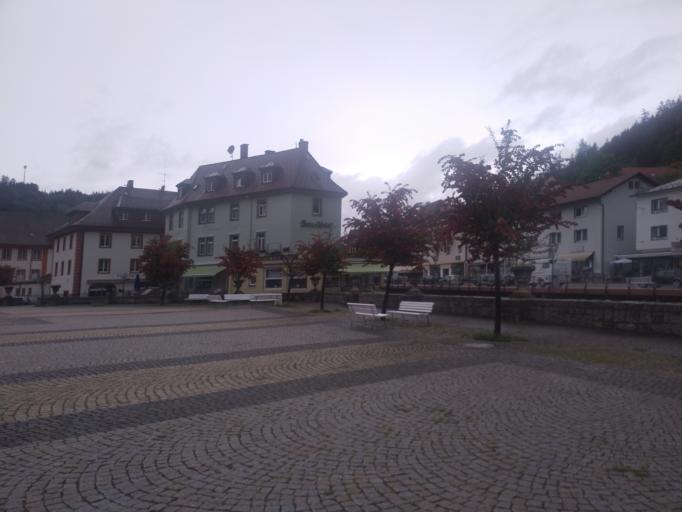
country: DE
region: Baden-Wuerttemberg
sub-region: Freiburg Region
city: Sankt Blasien
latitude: 47.7608
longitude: 8.1306
